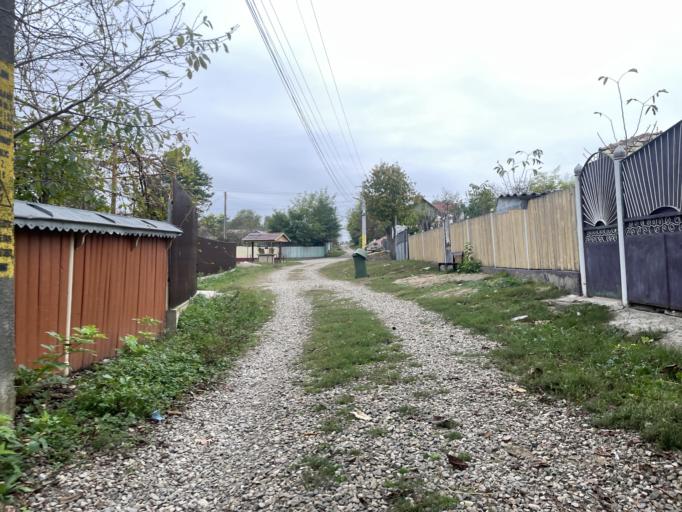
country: RO
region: Iasi
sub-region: Comuna Dumesti
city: Dumesti
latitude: 47.1727
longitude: 27.3441
